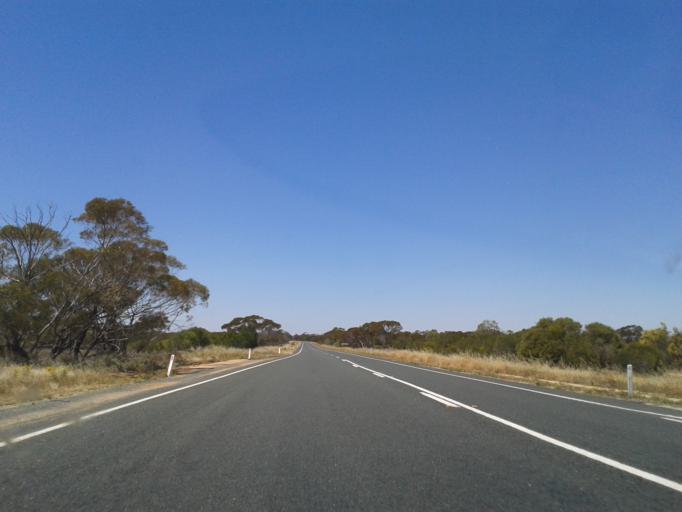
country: AU
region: New South Wales
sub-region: Wentworth
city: Gol Gol
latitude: -34.3127
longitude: 142.3540
